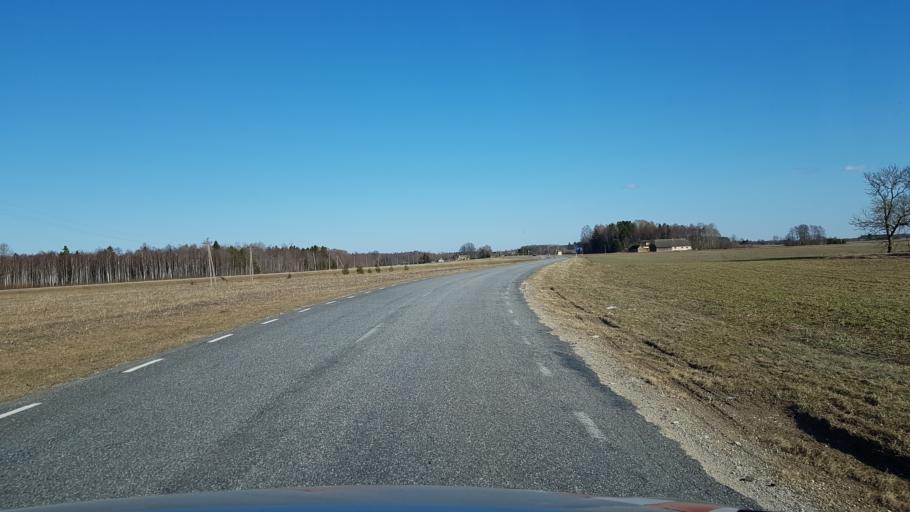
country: EE
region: Laeaene-Virumaa
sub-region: Haljala vald
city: Haljala
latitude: 59.4636
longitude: 26.1921
